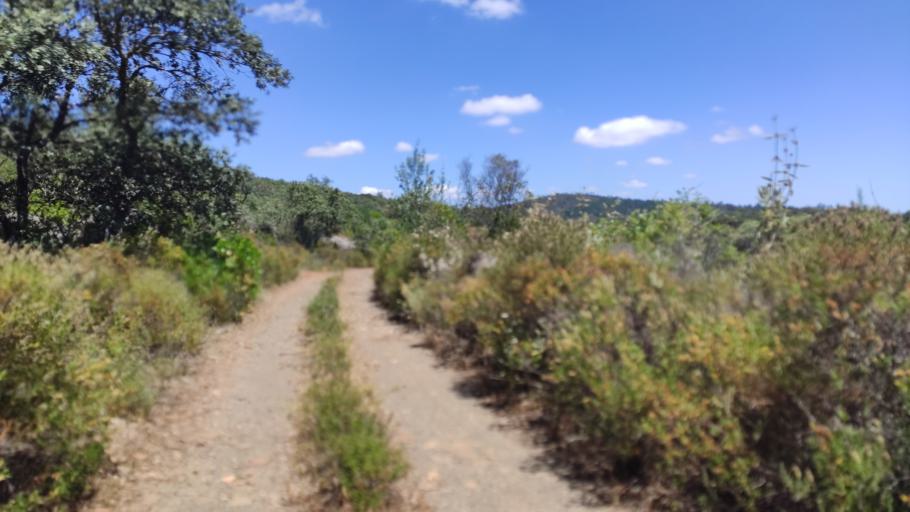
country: PT
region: Faro
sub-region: Sao Bras de Alportel
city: Sao Bras de Alportel
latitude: 37.1646
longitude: -7.9318
